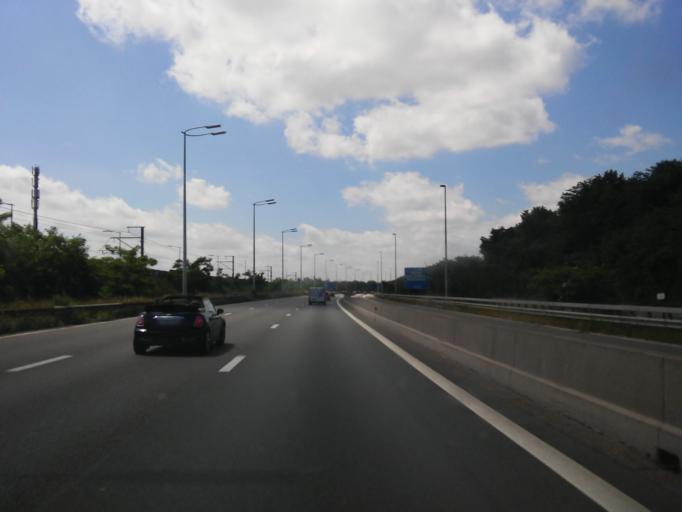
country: BE
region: Flanders
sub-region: Provincie Vlaams-Brabant
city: Machelen
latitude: 50.9125
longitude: 4.4553
